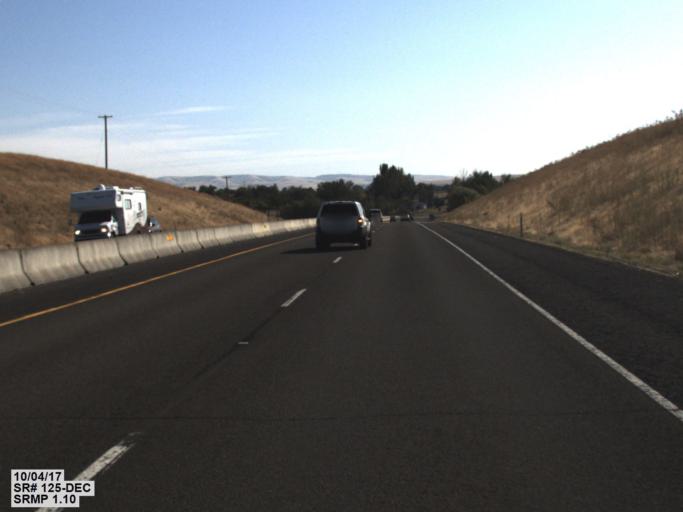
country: US
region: Washington
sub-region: Walla Walla County
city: College Place
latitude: 46.0163
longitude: -118.3892
